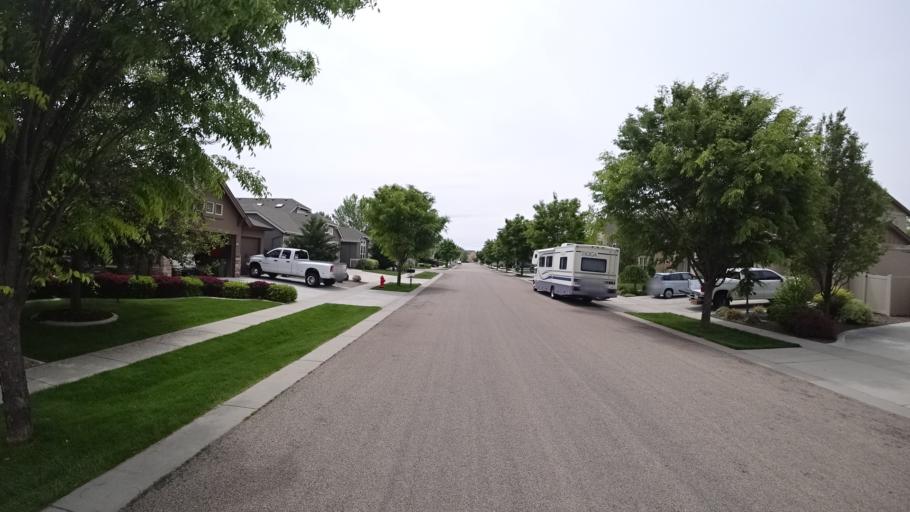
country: US
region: Idaho
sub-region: Ada County
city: Meridian
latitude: 43.5667
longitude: -116.3643
